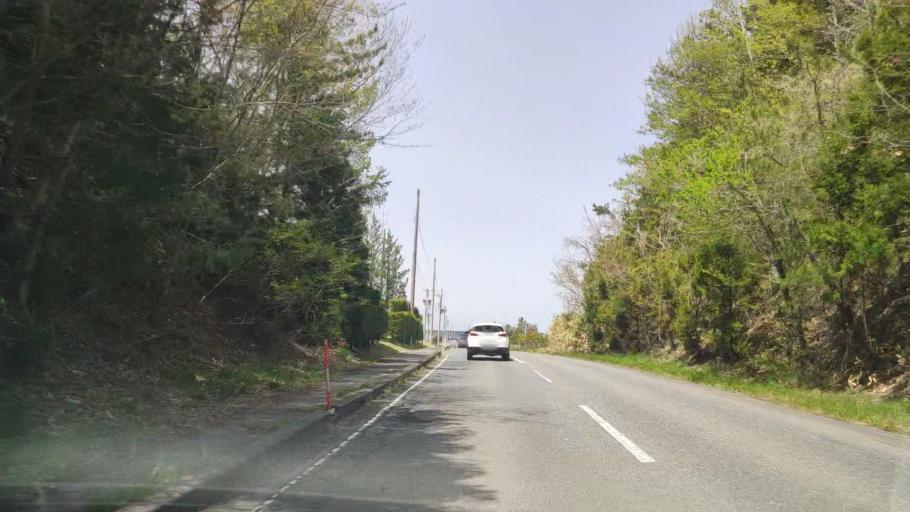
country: JP
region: Aomori
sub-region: Misawa Shi
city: Inuotose
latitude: 40.5895
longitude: 141.3513
